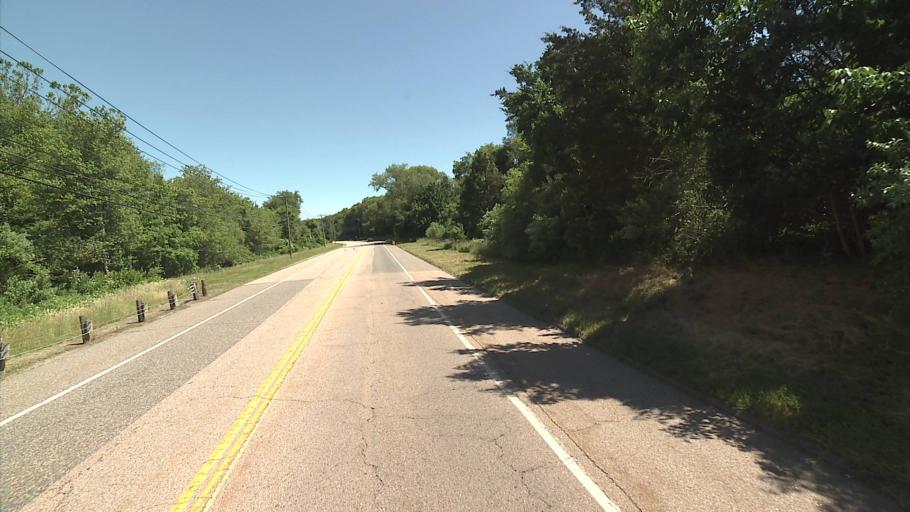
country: US
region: Connecticut
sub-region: New London County
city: Pawcatuck
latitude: 41.4151
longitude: -71.8452
